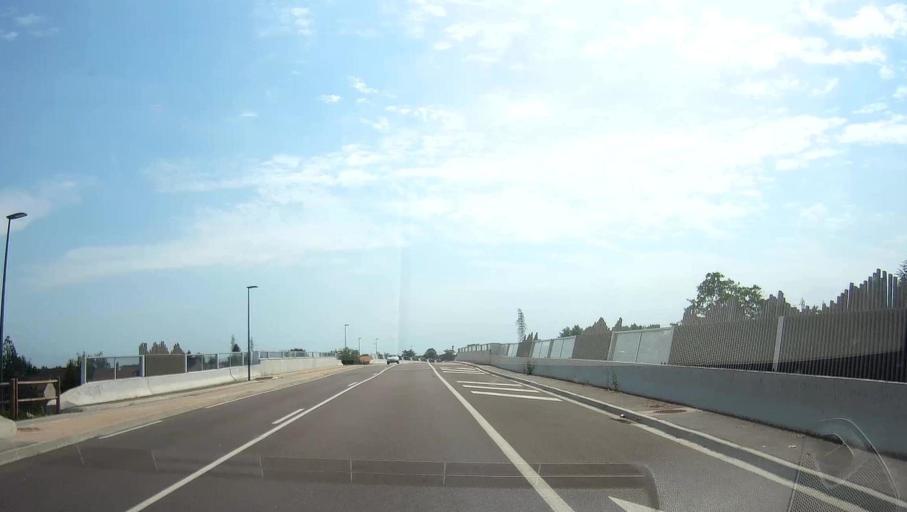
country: FR
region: Bourgogne
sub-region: Departement de la Cote-d'Or
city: Beaune
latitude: 47.0323
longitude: 4.8576
